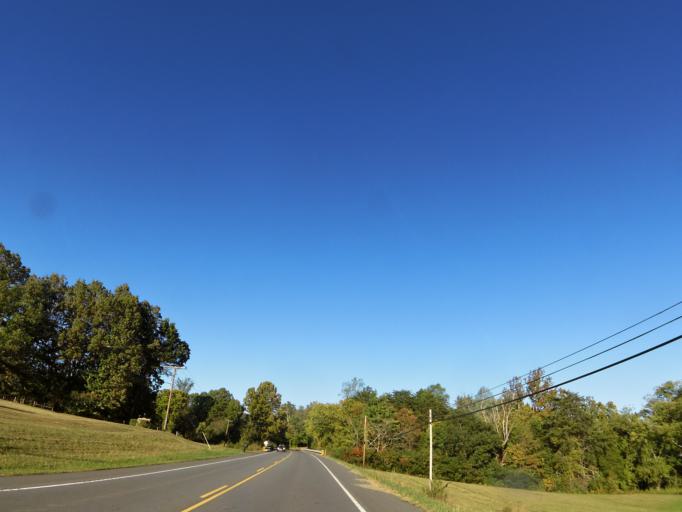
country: US
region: Tennessee
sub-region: Grainger County
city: Bean Station
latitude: 36.3246
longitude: -83.3814
